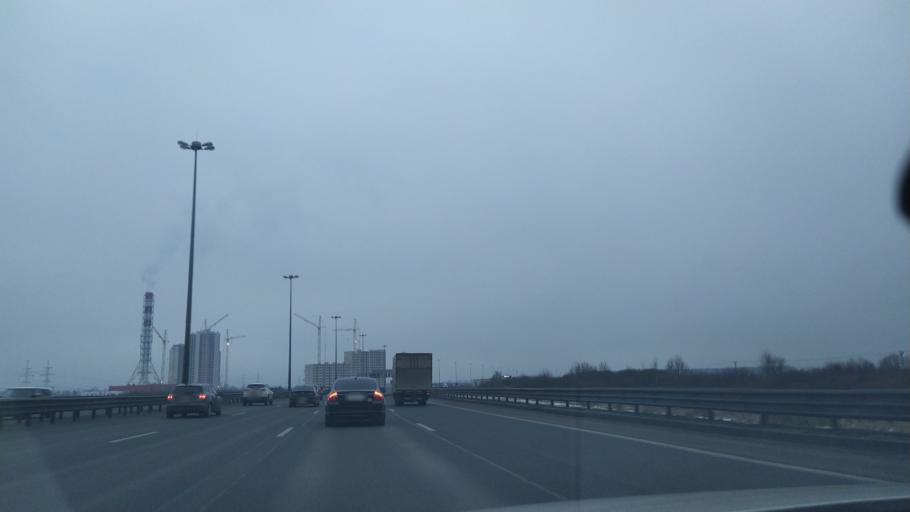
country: RU
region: St.-Petersburg
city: Krasnogvargeisky
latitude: 60.0099
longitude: 30.4748
